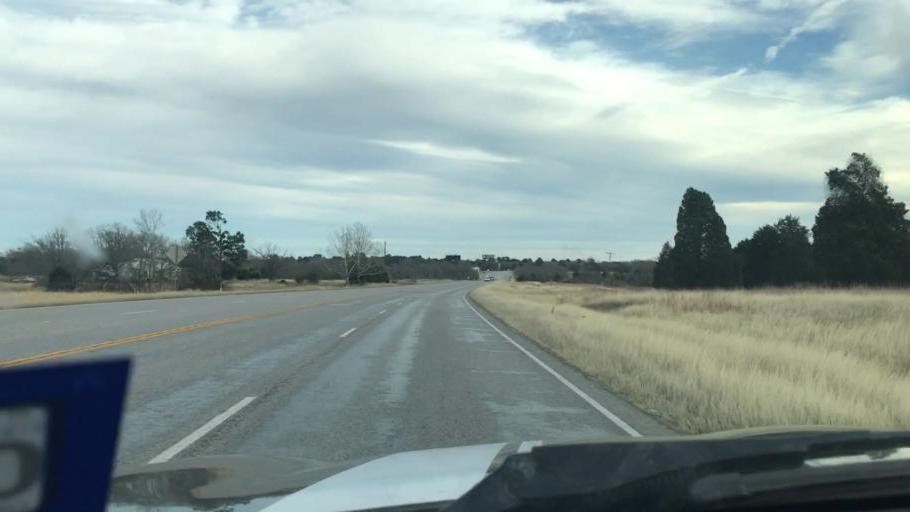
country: US
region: Texas
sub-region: Bastrop County
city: Camp Swift
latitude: 30.2965
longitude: -97.2682
